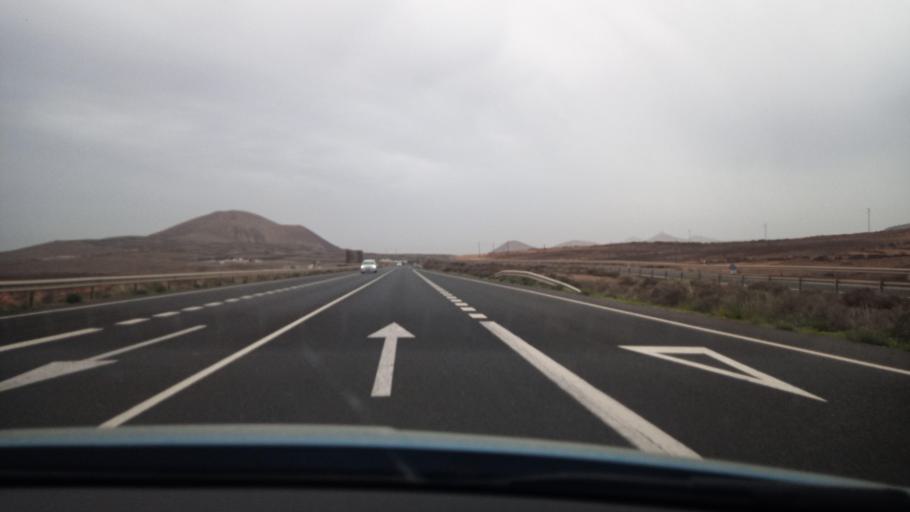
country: ES
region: Canary Islands
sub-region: Provincia de Las Palmas
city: Nazaret
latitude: 29.0297
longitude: -13.5241
